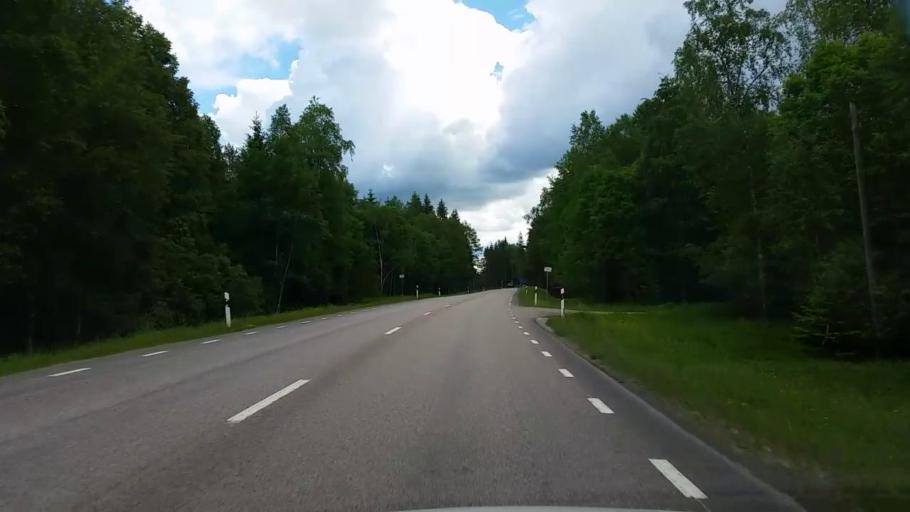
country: SE
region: Vaestmanland
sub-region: Norbergs Kommun
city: Norberg
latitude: 60.0749
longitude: 15.9631
